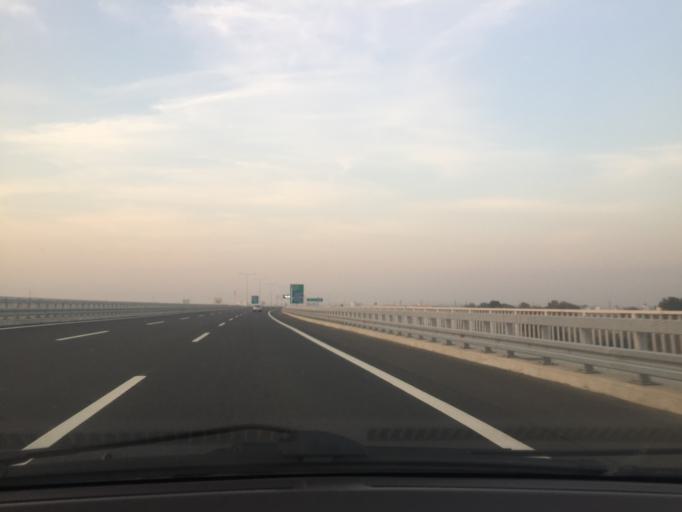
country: TR
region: Bursa
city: Karacabey
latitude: 40.2010
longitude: 28.3738
